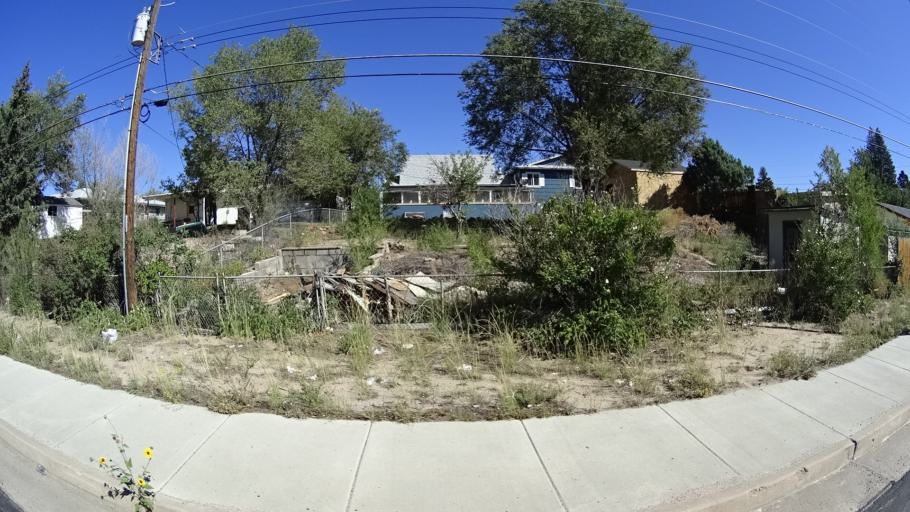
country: US
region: Colorado
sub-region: El Paso County
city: Cimarron Hills
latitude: 38.8545
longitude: -104.7600
